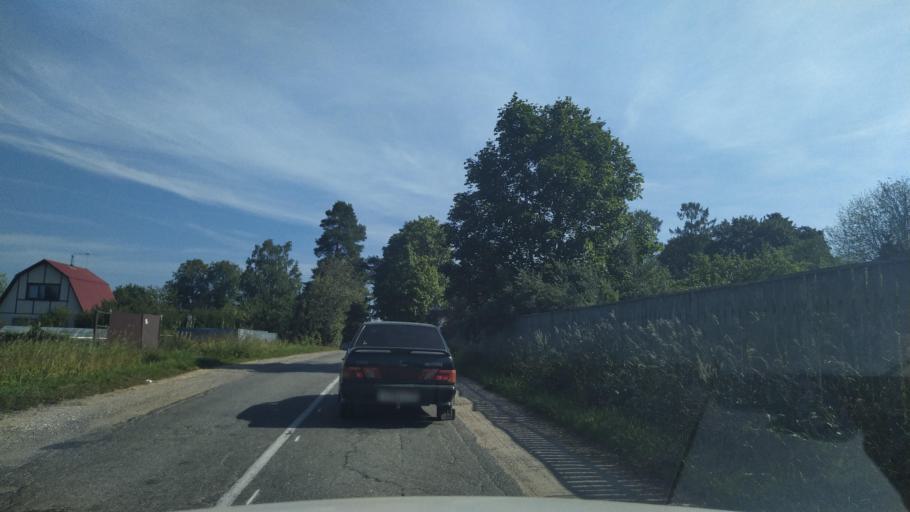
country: RU
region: Leningrad
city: Siverskiy
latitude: 59.3299
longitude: 30.0340
